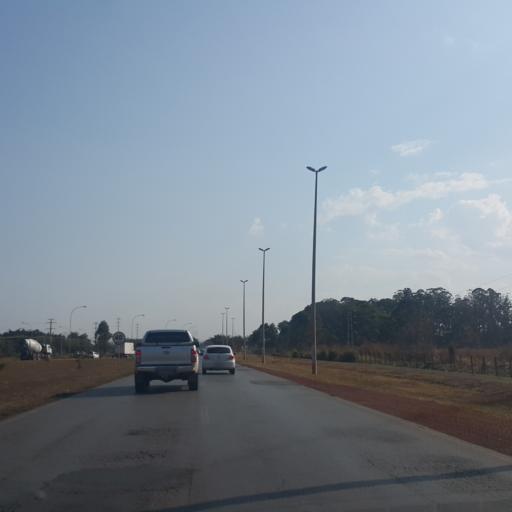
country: BR
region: Federal District
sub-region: Brasilia
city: Brasilia
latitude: -15.8728
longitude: -48.0441
